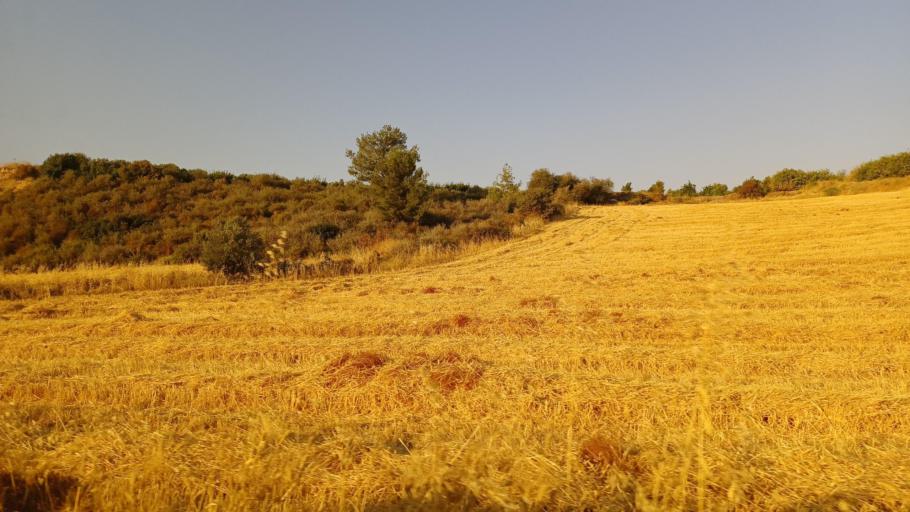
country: CY
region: Pafos
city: Polis
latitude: 35.0465
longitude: 32.4597
